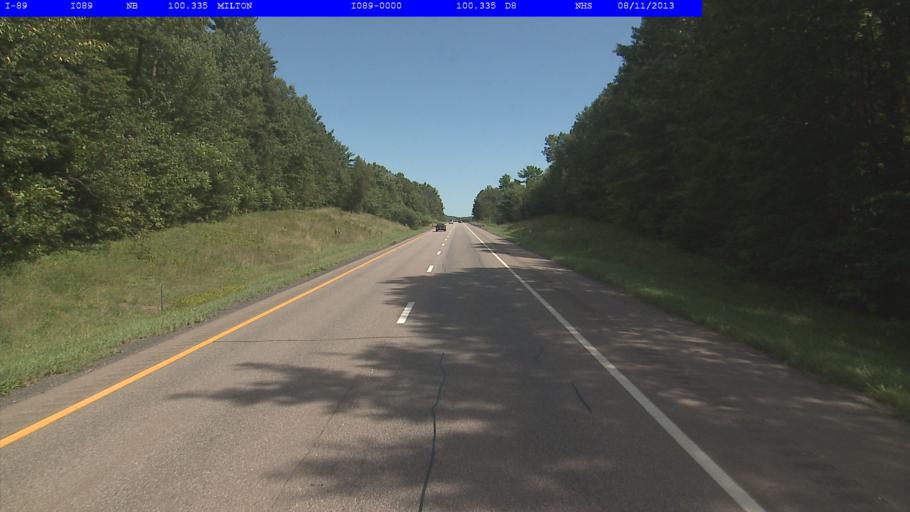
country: US
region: Vermont
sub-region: Chittenden County
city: Milton
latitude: 44.6220
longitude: -73.1554
